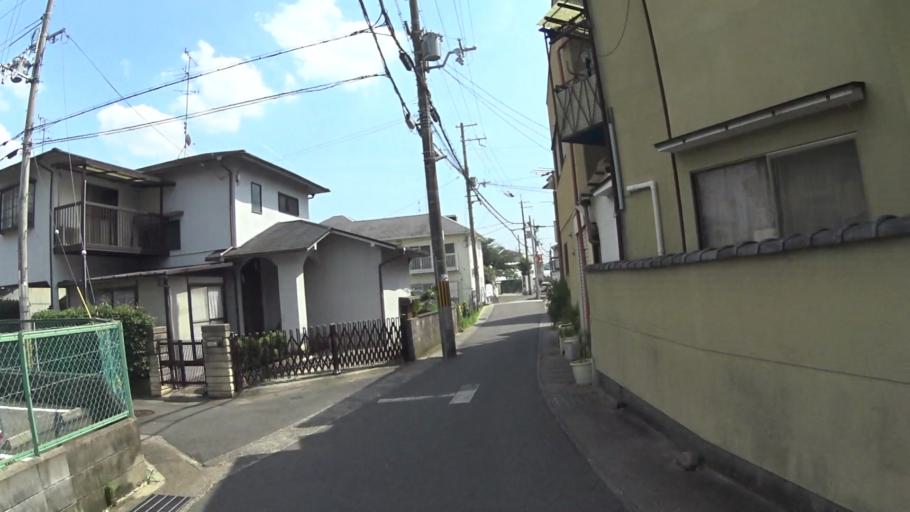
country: JP
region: Kyoto
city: Muko
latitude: 35.0068
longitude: 135.6941
